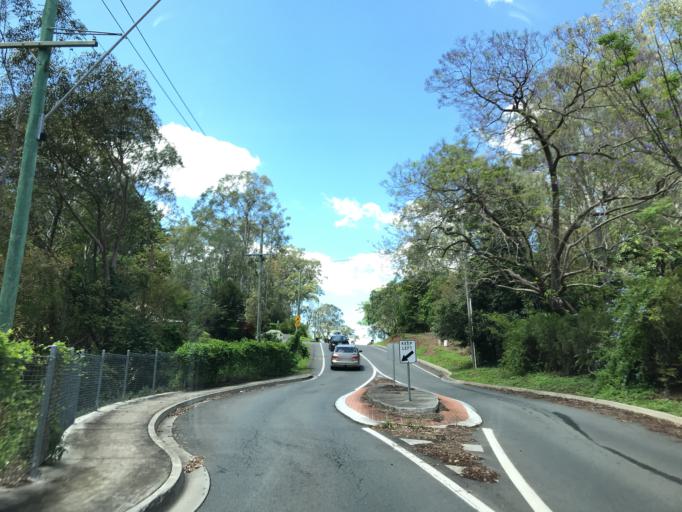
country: AU
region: Queensland
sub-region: Brisbane
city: Kenmore Hills
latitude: -27.4923
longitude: 152.9251
